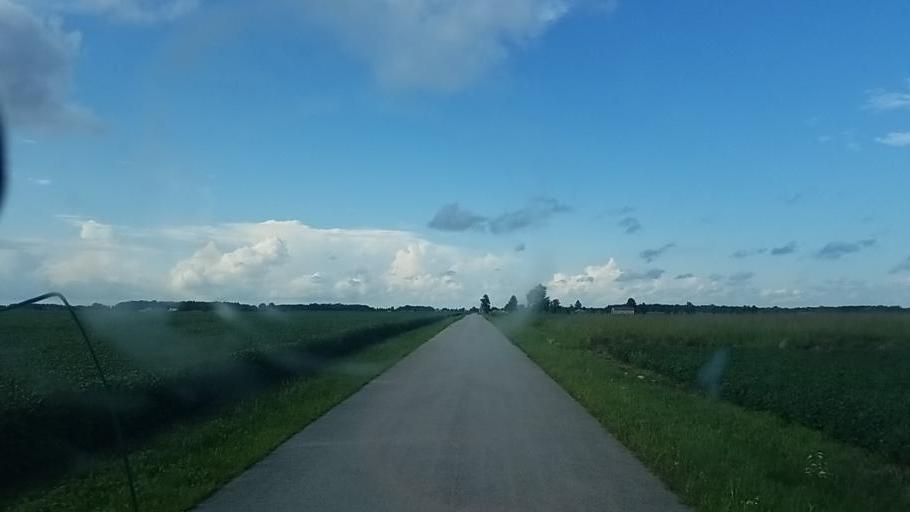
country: US
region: Ohio
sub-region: Hardin County
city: Forest
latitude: 40.7628
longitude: -83.4488
